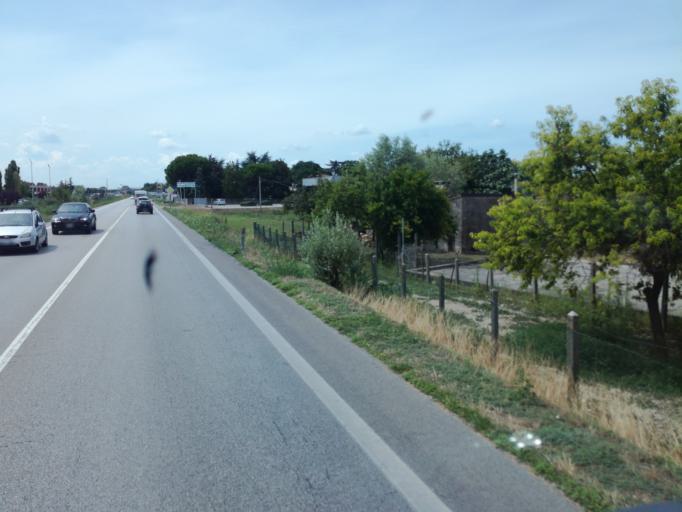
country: IT
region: Veneto
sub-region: Provincia di Rovigo
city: Taglio di Po
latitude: 45.0021
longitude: 12.2245
